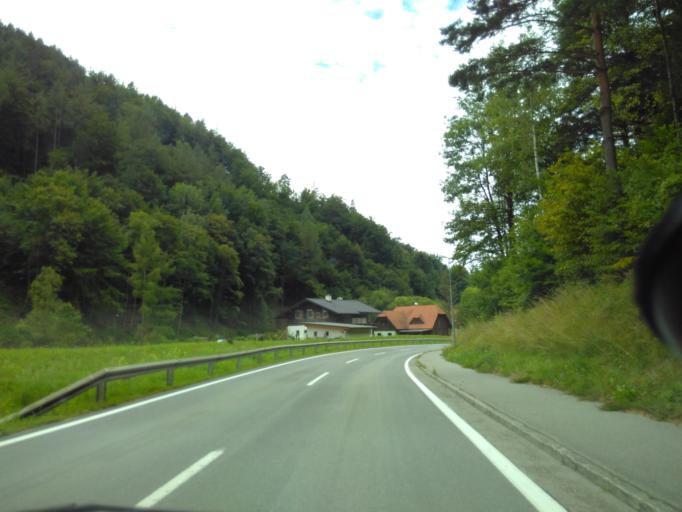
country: AT
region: Styria
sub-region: Politischer Bezirk Graz-Umgebung
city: Schrems bei Frohnleiten
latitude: 47.2707
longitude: 15.3401
